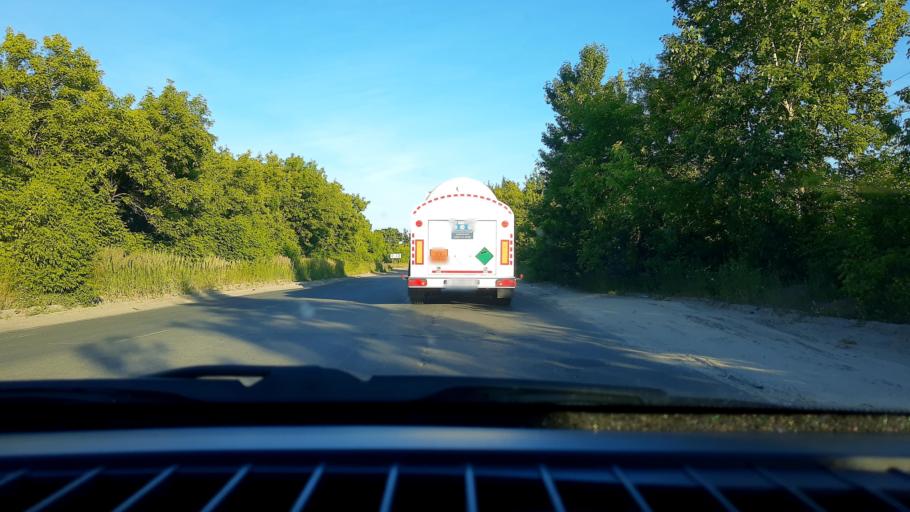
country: RU
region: Nizjnij Novgorod
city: Dzerzhinsk
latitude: 56.2489
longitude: 43.4982
